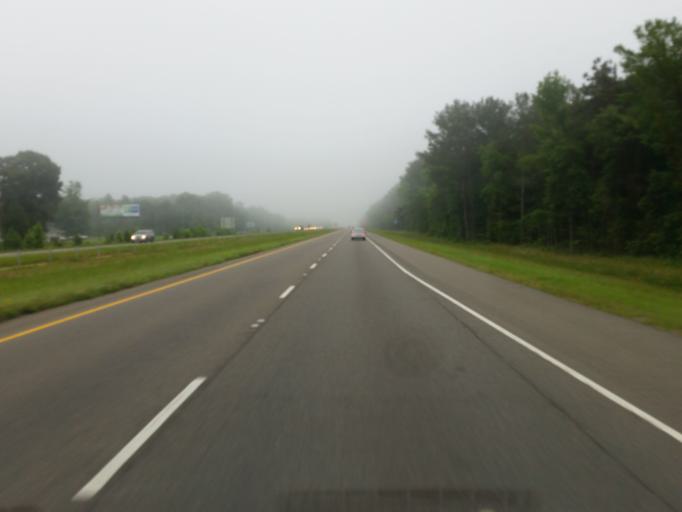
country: US
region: Louisiana
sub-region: Bossier Parish
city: Haughton
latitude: 32.5795
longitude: -93.4244
